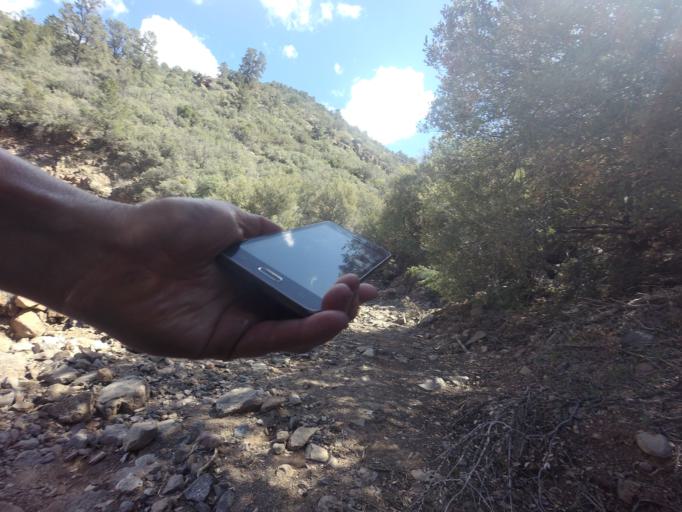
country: US
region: Arizona
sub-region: Gila County
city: Pine
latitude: 34.4014
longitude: -111.5969
